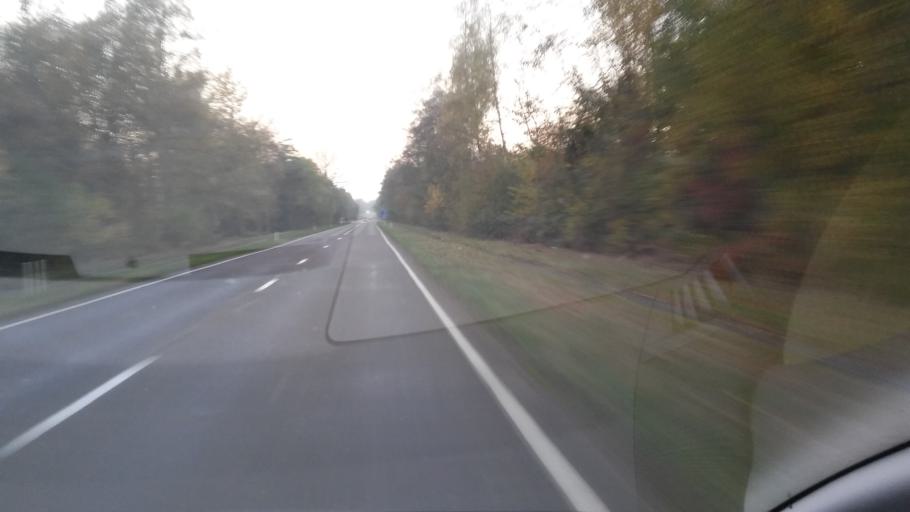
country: BE
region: Wallonia
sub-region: Province du Luxembourg
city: Etalle
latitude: 49.6717
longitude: 5.6461
